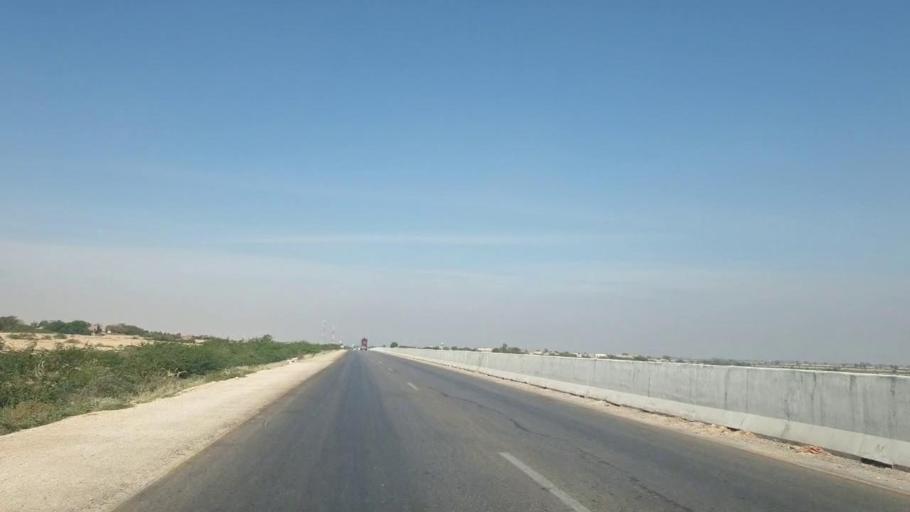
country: PK
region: Sindh
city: Hala
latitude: 25.6915
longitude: 68.2954
